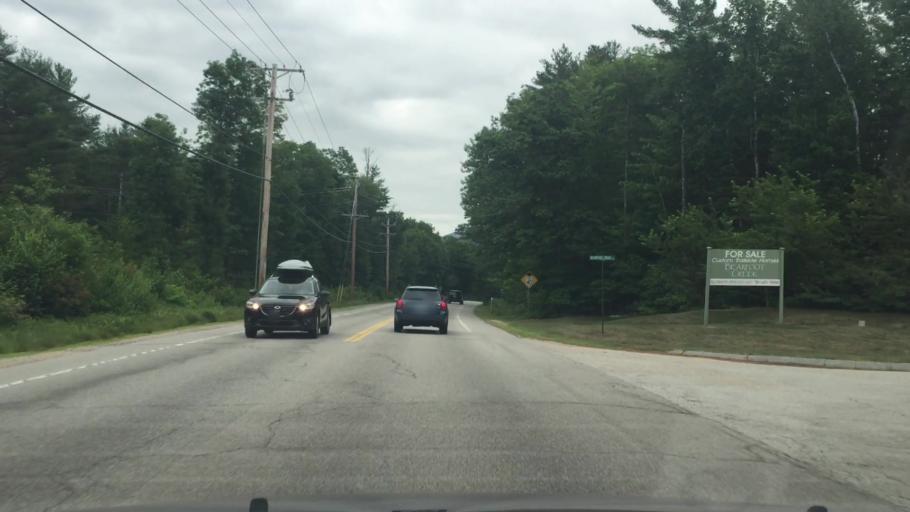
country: US
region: New Hampshire
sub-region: Carroll County
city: North Conway
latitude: 44.0819
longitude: -71.2401
